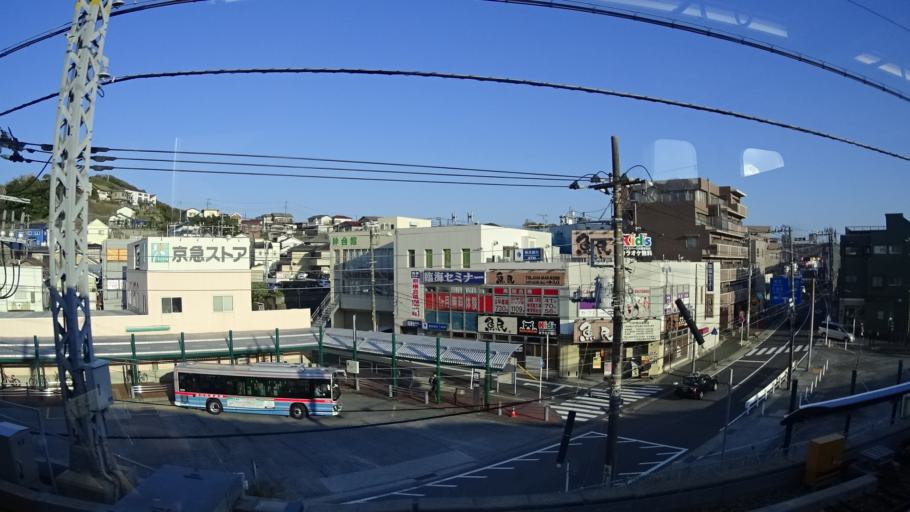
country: JP
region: Kanagawa
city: Yokosuka
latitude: 35.2115
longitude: 139.6846
